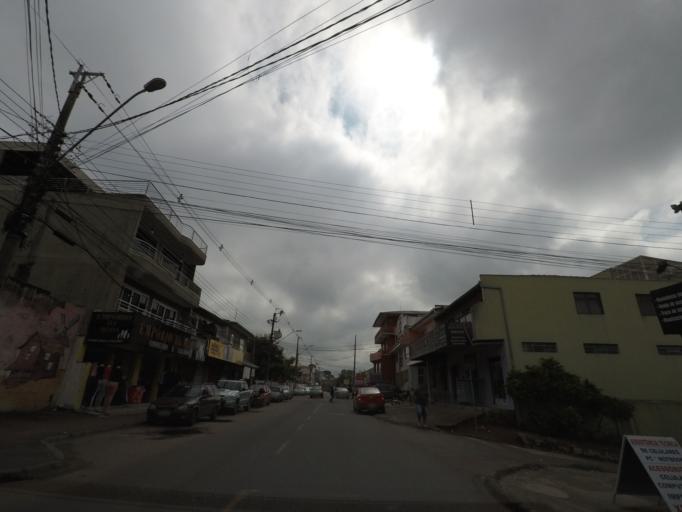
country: BR
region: Parana
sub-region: Curitiba
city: Curitiba
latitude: -25.4967
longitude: -49.3380
